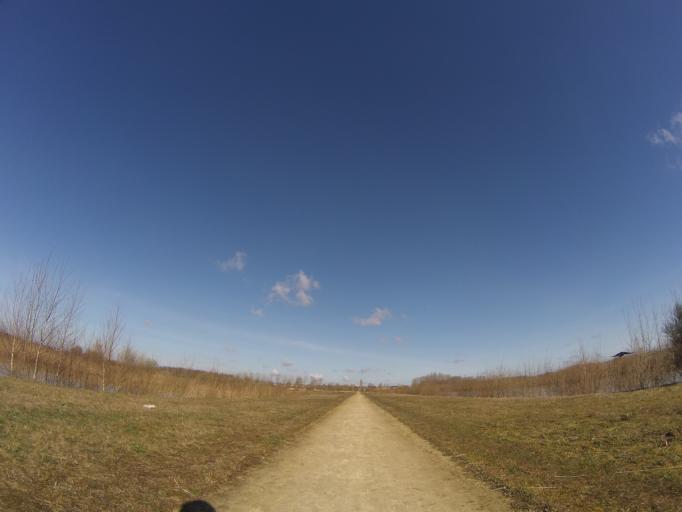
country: NL
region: Drenthe
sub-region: Gemeente Emmen
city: Emmen
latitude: 52.7329
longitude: 6.8896
